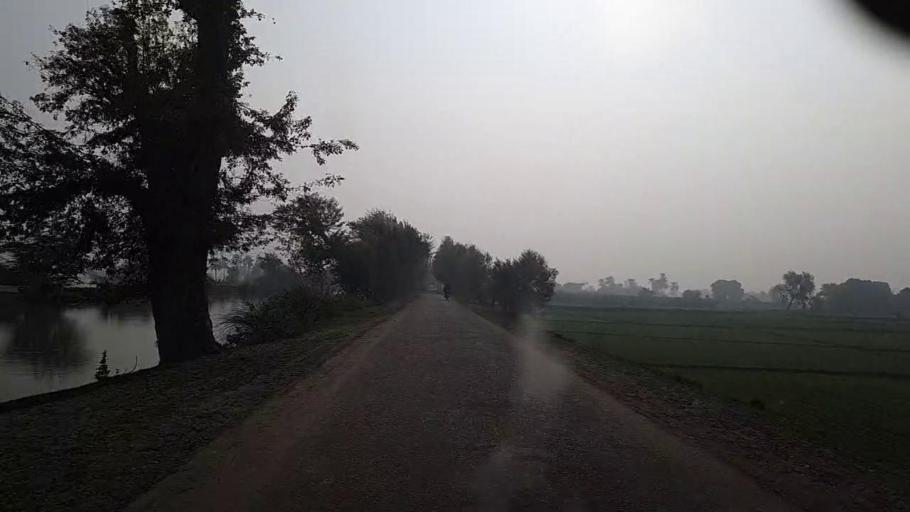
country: PK
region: Sindh
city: Bozdar
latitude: 27.1475
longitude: 68.6599
